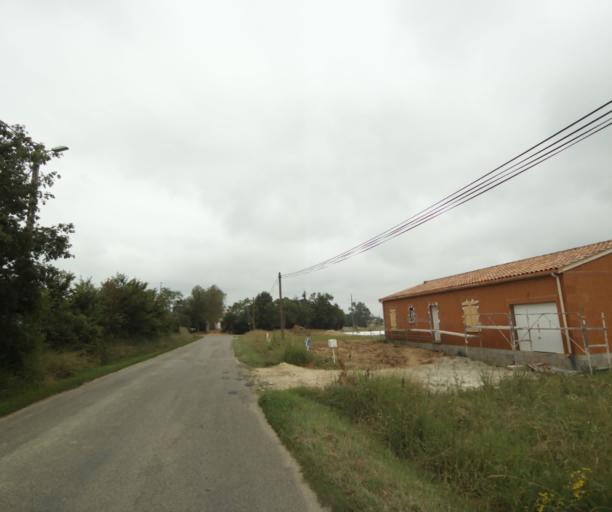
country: FR
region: Midi-Pyrenees
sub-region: Departement du Tarn-et-Garonne
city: Montbeton
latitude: 43.9909
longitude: 1.3063
